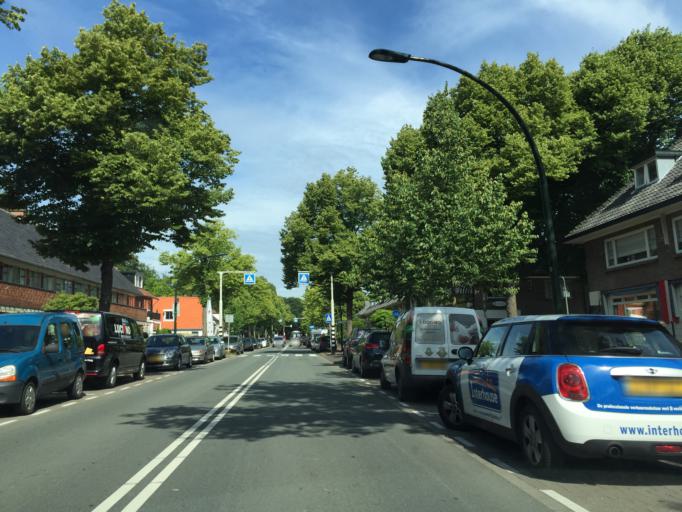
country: NL
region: South Holland
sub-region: Gemeente Wassenaar
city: Wassenaar
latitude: 52.1474
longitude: 4.3935
